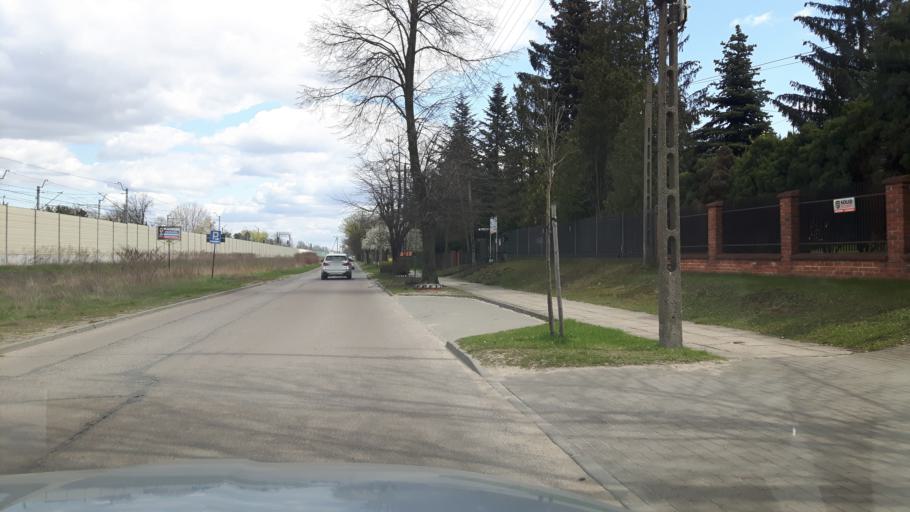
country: PL
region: Masovian Voivodeship
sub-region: Powiat wolominski
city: Kobylka
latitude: 52.3370
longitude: 21.2169
